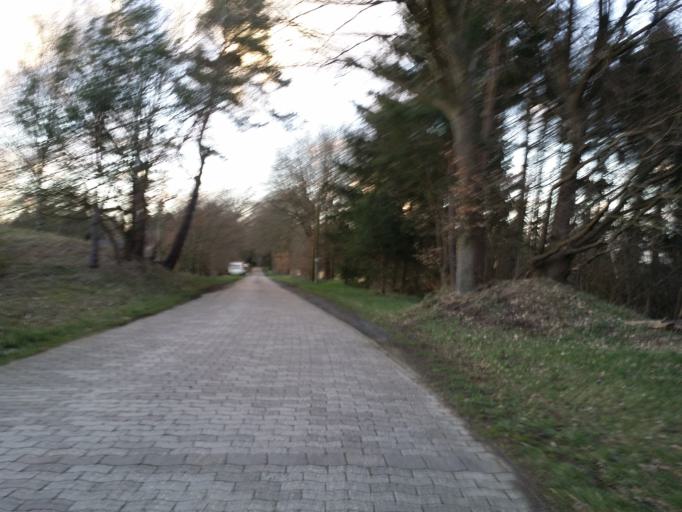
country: DE
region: Lower Saxony
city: Gross Ippener
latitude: 52.9736
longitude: 8.5978
